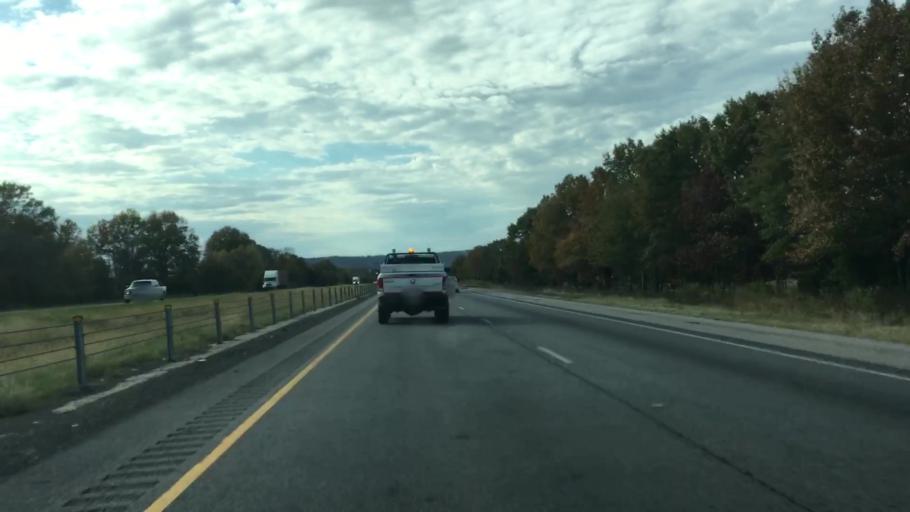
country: US
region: Arkansas
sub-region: Pope County
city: Atkins
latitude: 35.2482
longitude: -92.8746
